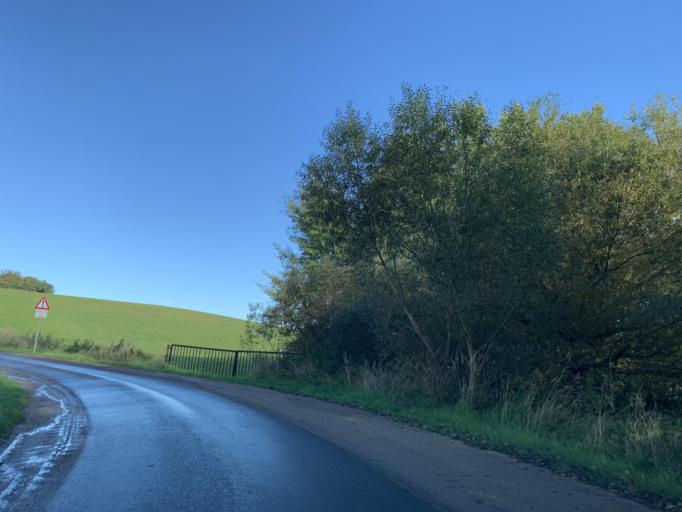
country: DE
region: Mecklenburg-Vorpommern
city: Burg Stargard
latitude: 53.4567
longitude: 13.2831
